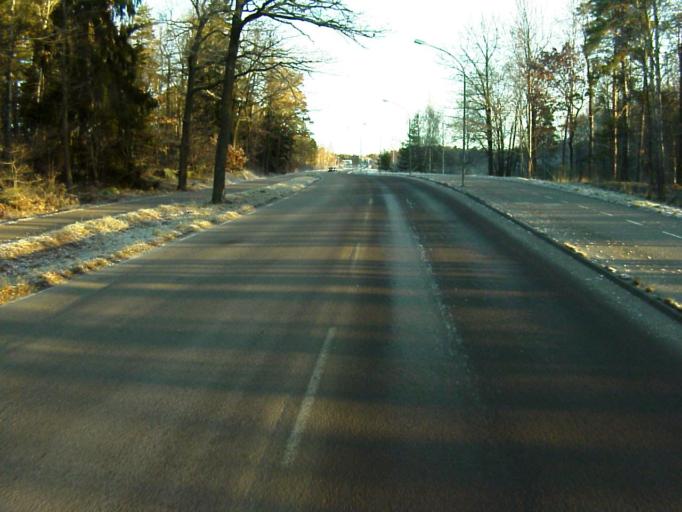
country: SE
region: Soedermanland
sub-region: Eskilstuna Kommun
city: Eskilstuna
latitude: 59.3538
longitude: 16.4831
